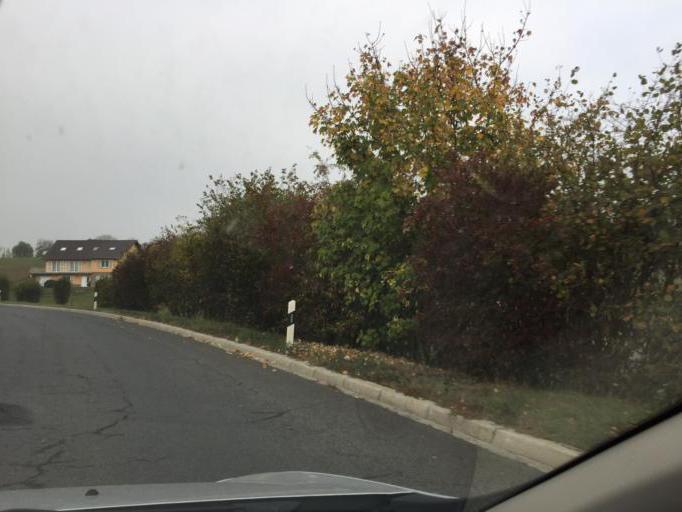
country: LU
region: Grevenmacher
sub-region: Canton de Remich
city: Bous
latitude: 49.5534
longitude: 6.3223
